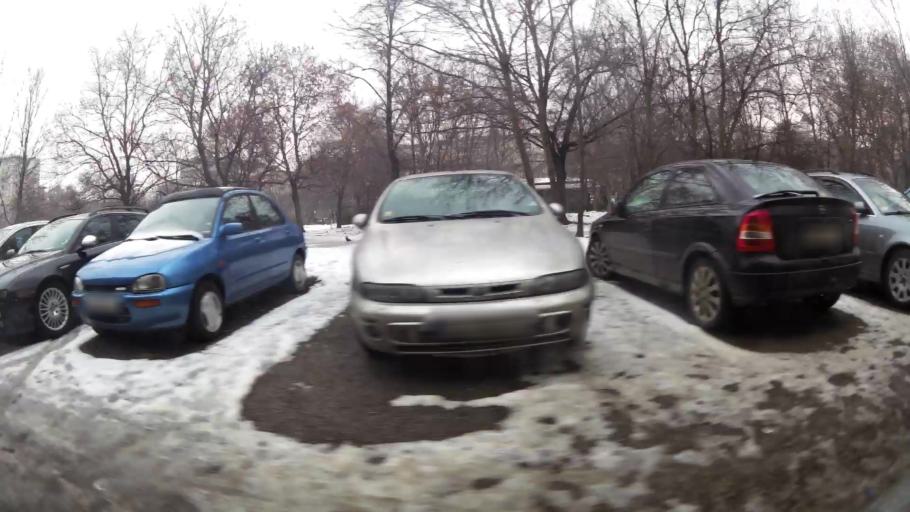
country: BG
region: Sofia-Capital
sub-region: Stolichna Obshtina
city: Sofia
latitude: 42.6797
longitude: 23.2970
